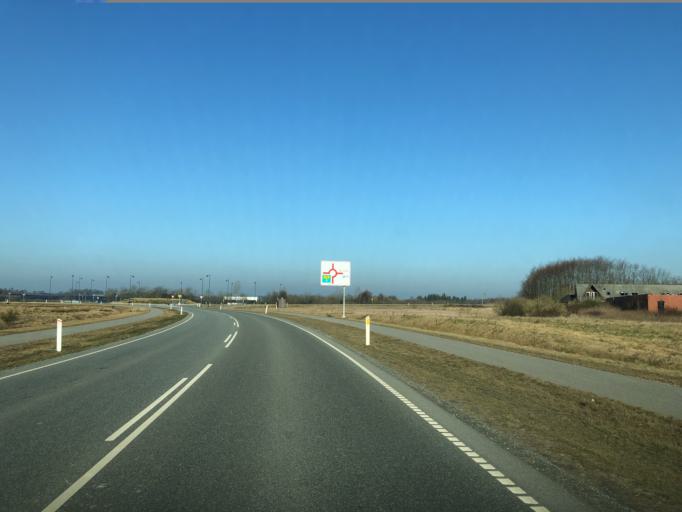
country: DK
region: Central Jutland
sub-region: Silkeborg Kommune
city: Silkeborg
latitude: 56.2024
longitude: 9.5568
